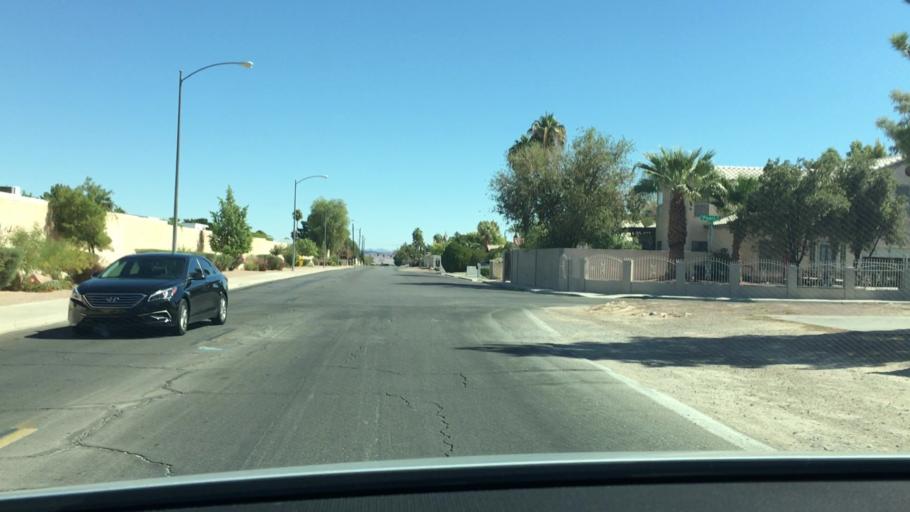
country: US
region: Nevada
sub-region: Clark County
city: Winchester
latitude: 36.1189
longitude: -115.0970
